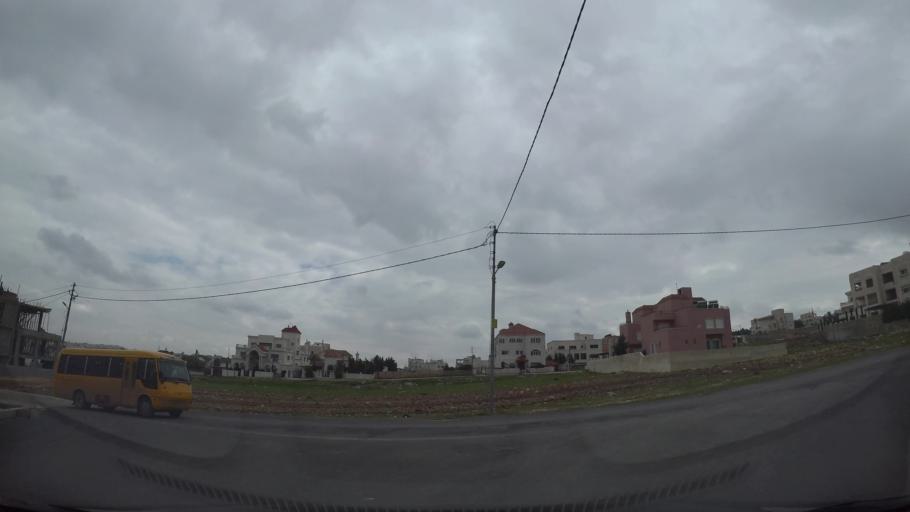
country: JO
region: Amman
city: Umm as Summaq
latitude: 31.9262
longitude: 35.8545
